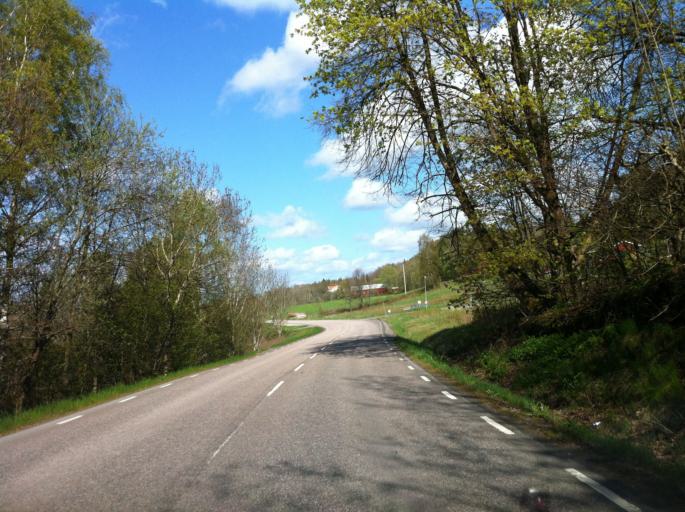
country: SE
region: Vaestra Goetaland
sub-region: Alingsas Kommun
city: Alingsas
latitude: 57.8599
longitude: 12.5606
